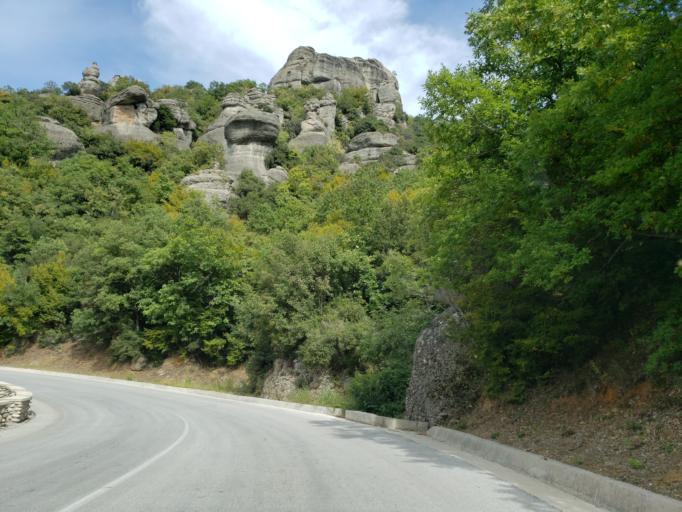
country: GR
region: Thessaly
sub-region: Trikala
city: Kastraki
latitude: 39.7197
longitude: 21.6334
